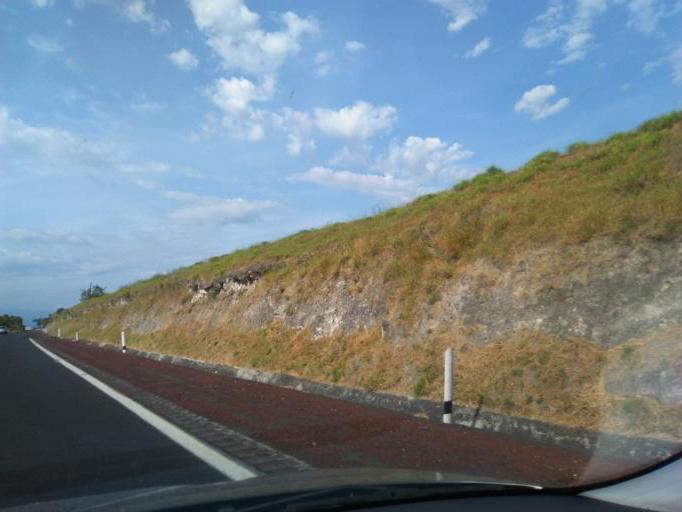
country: MX
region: Morelos
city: Puente de Ixtla
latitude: 18.6395
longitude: -99.2954
